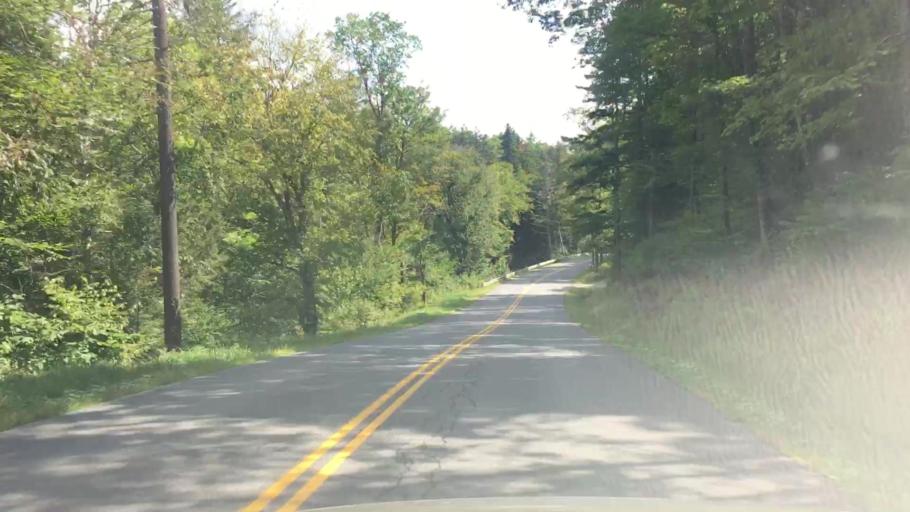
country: US
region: Vermont
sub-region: Windham County
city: Dover
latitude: 42.8176
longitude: -72.7554
